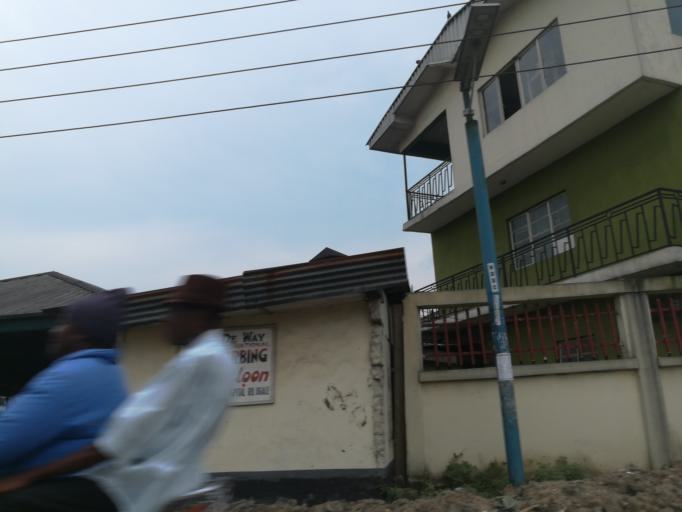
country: NG
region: Rivers
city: Okrika
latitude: 4.7877
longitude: 7.1255
